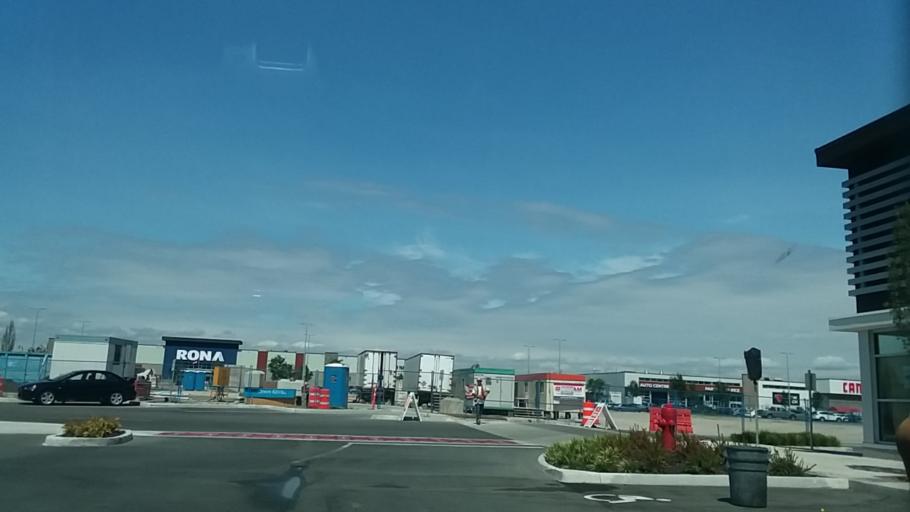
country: CA
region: British Columbia
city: Ladner
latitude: 49.0409
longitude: -123.0893
